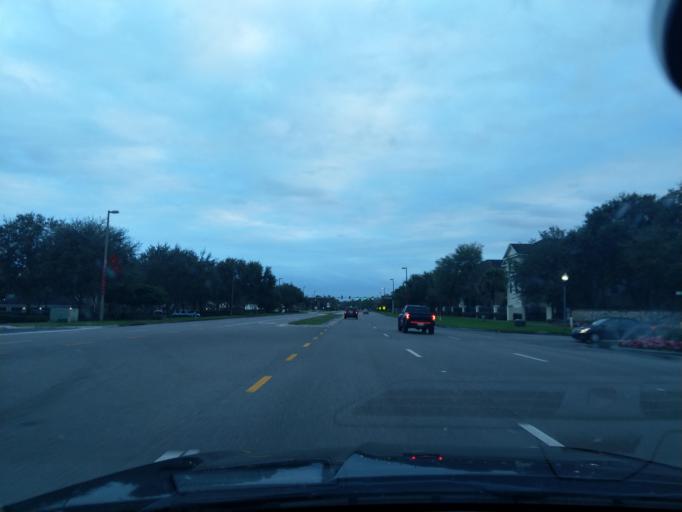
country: US
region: Florida
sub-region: Orange County
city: Williamsburg
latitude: 28.3806
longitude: -81.4874
